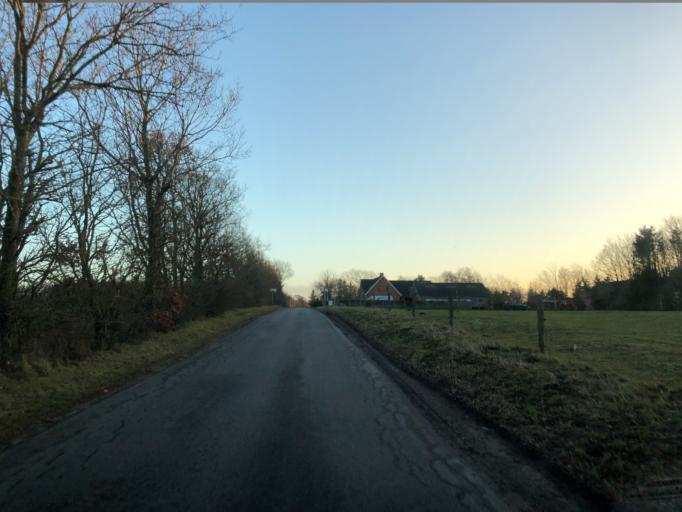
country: DK
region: Central Jutland
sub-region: Skive Kommune
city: Skive
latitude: 56.5410
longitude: 8.9313
